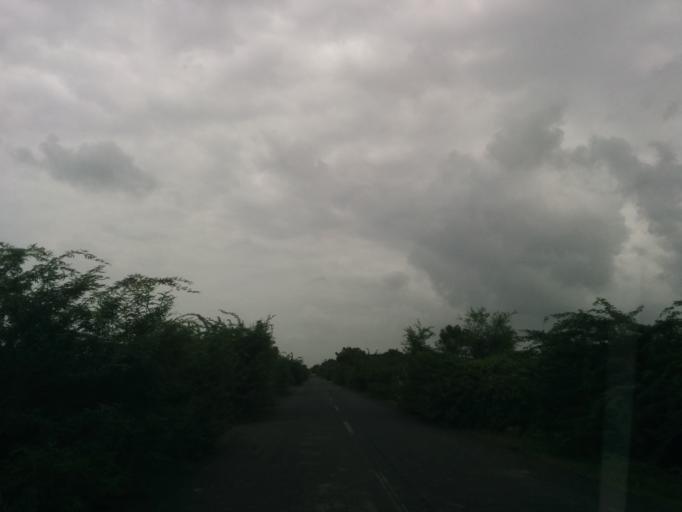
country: IN
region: Gujarat
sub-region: Ahmadabad
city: Sanand
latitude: 23.0683
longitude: 72.3933
